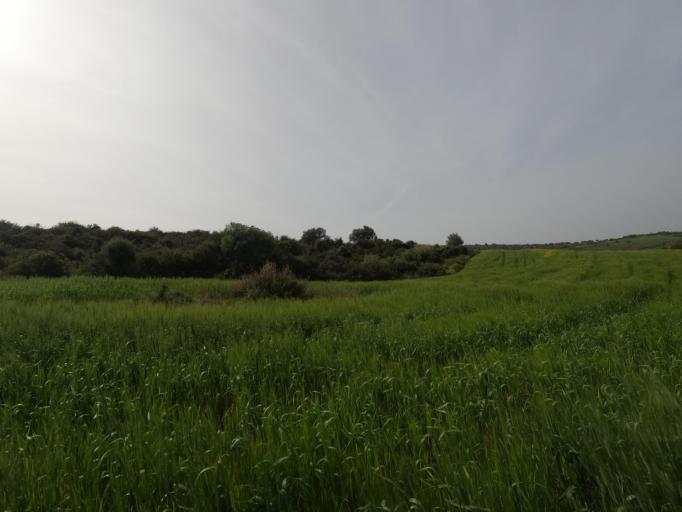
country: CY
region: Pafos
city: Pegeia
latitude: 34.9476
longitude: 32.3573
